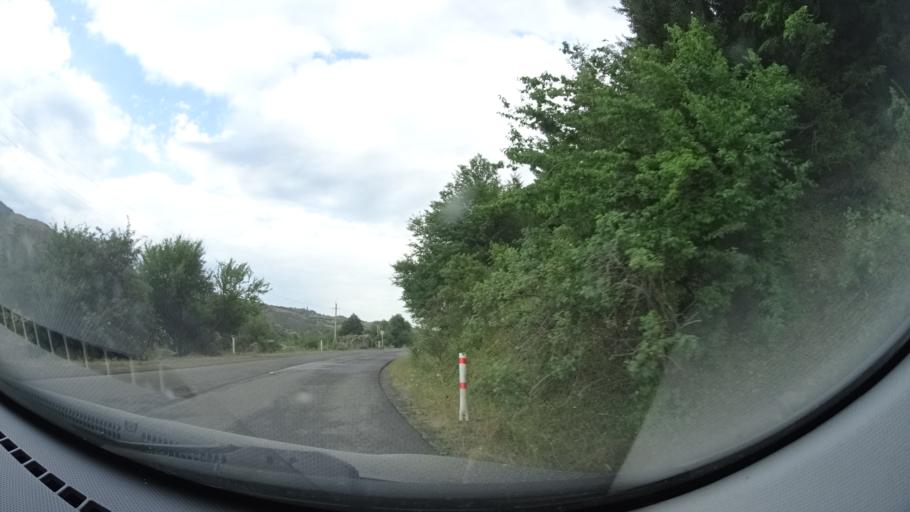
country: GE
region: Samtskhe-Javakheti
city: Adigeni
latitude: 41.6798
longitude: 42.6730
